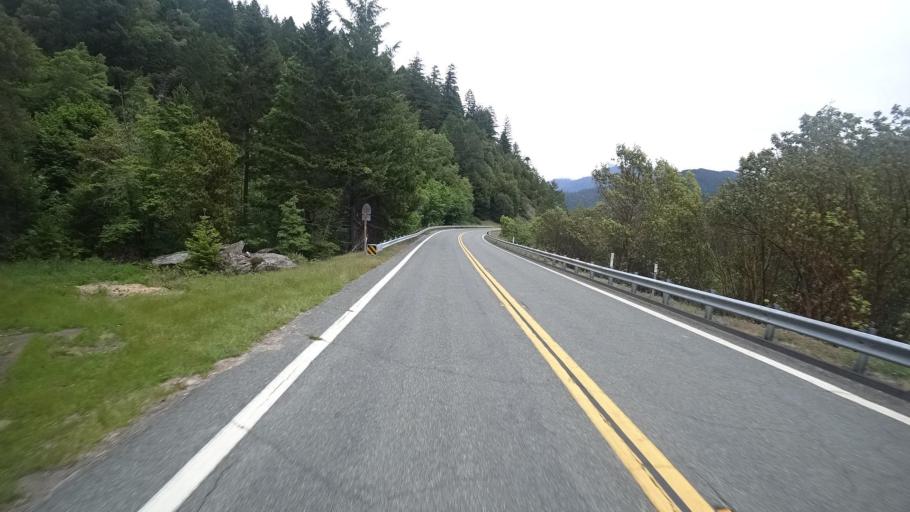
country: US
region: California
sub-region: Humboldt County
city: Willow Creek
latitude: 41.2774
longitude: -123.5944
